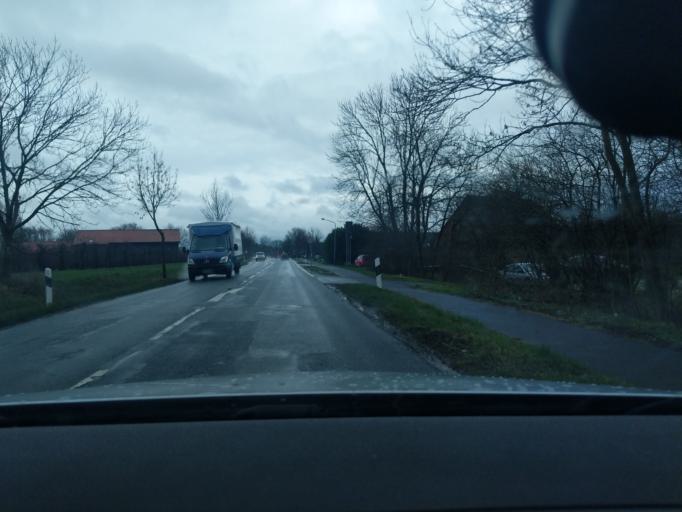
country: DE
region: Lower Saxony
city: Jork
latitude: 53.5520
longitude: 9.6634
